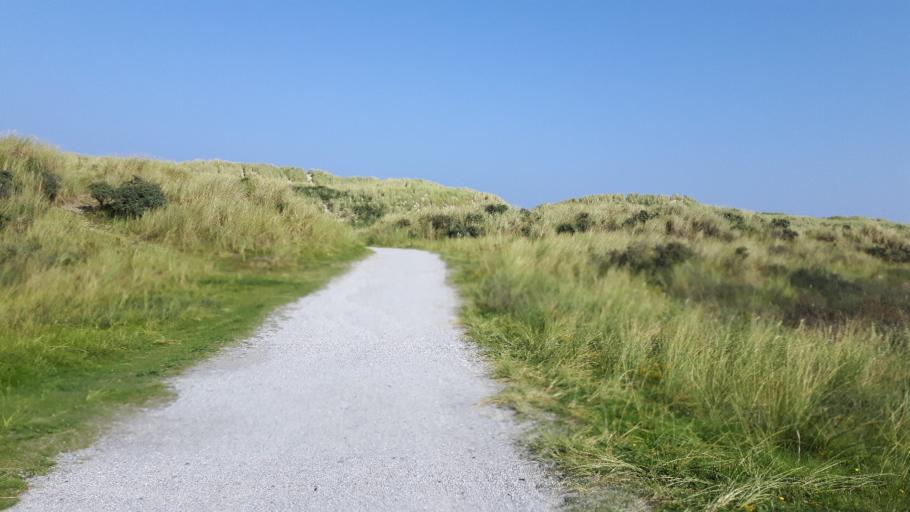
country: NL
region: Friesland
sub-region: Gemeente Ameland
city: Nes
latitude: 53.4608
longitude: 5.8170
